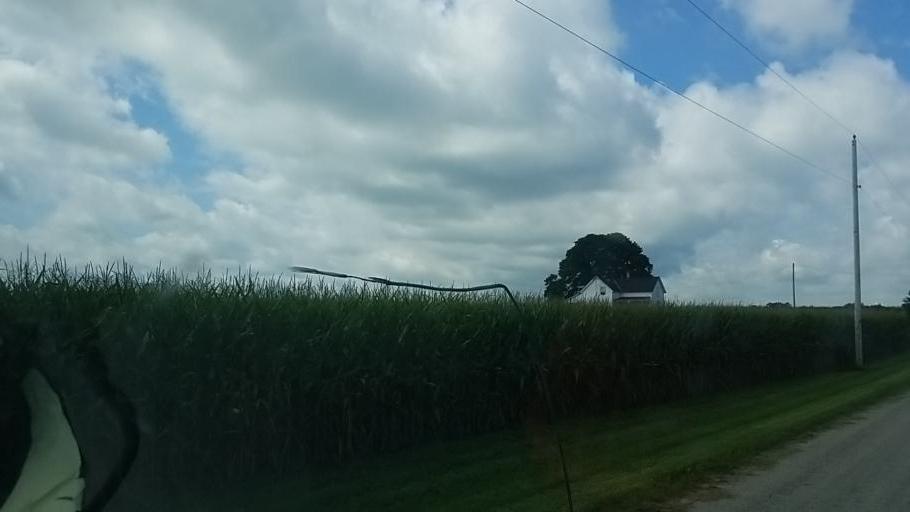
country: US
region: Ohio
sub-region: Madison County
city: Bethel
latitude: 39.7169
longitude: -83.4396
